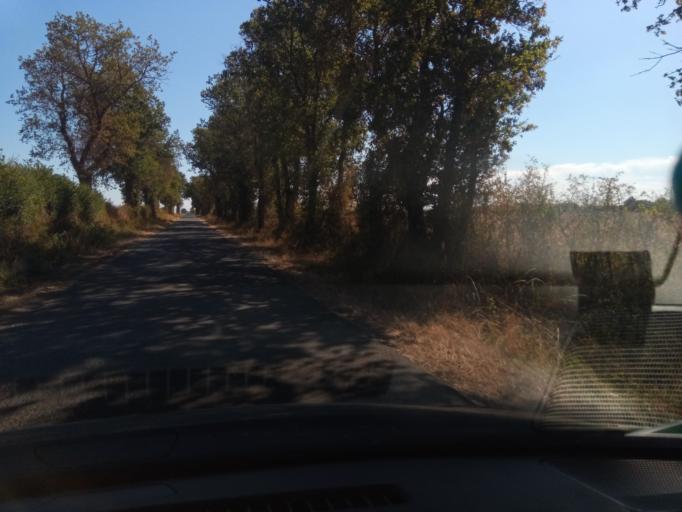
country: FR
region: Poitou-Charentes
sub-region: Departement de la Vienne
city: Saulge
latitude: 46.3783
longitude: 0.8004
